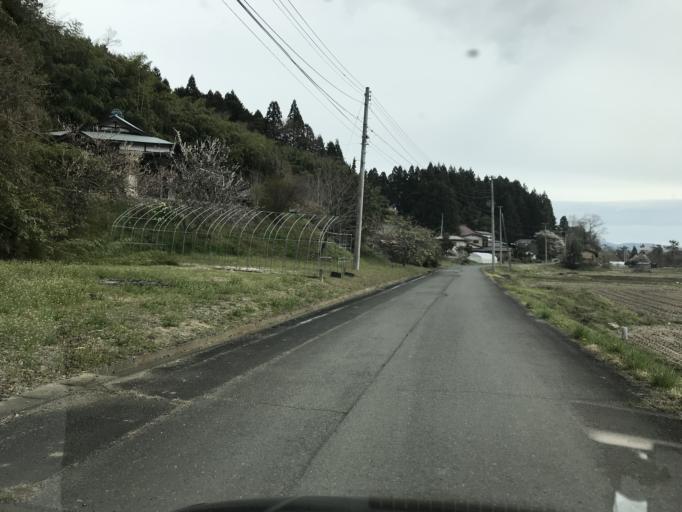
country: JP
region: Iwate
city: Ichinoseki
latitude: 38.9120
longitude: 141.0952
